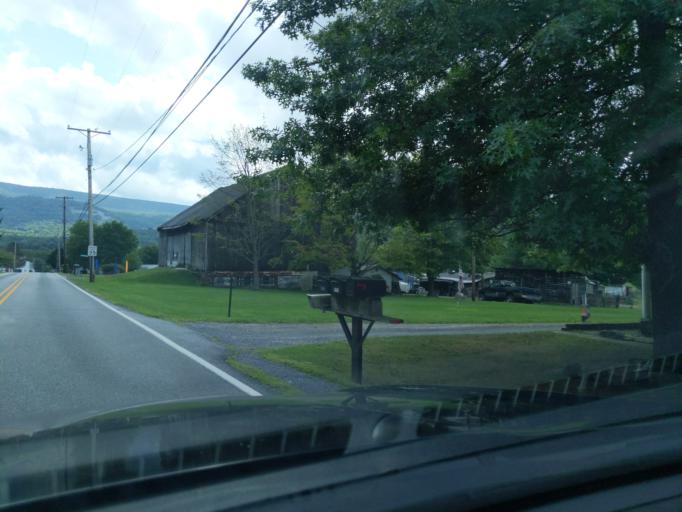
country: US
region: Pennsylvania
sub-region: Blair County
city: Duncansville
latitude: 40.3963
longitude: -78.4175
